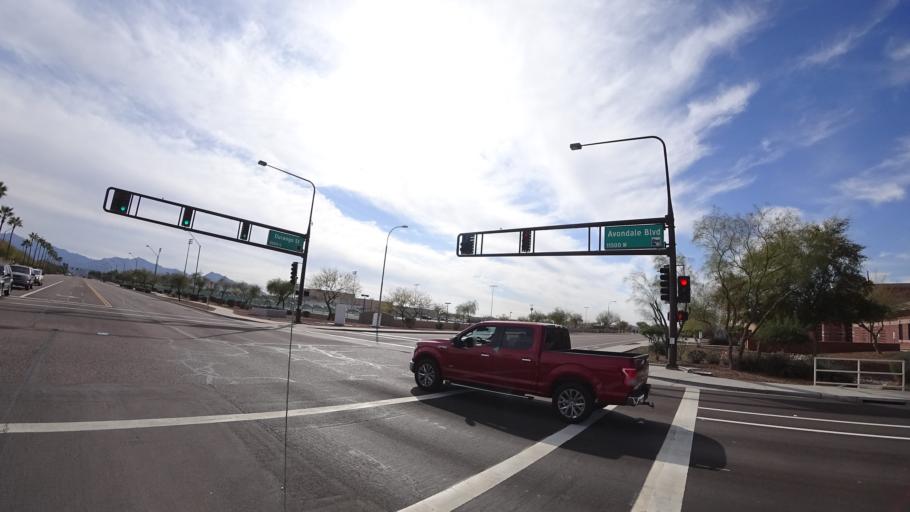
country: US
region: Arizona
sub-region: Maricopa County
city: Avondale
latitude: 33.4283
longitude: -112.3064
